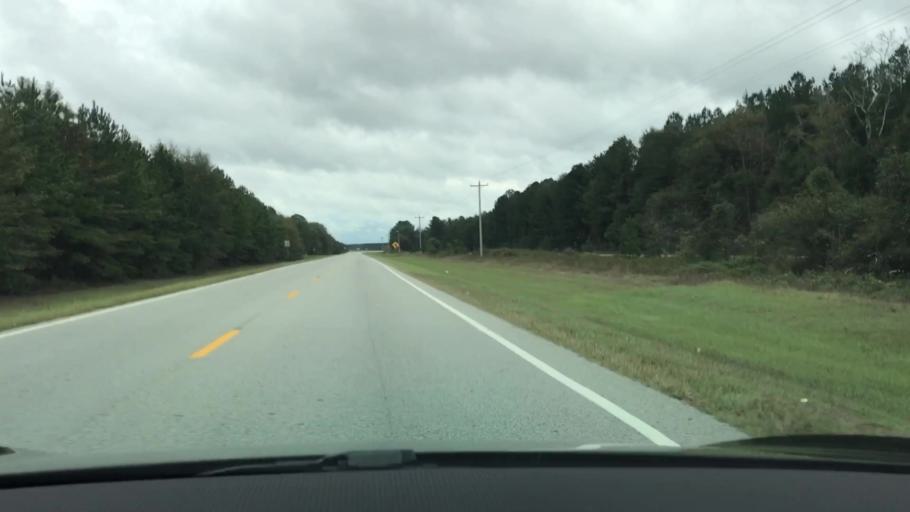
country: US
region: Georgia
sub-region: Glascock County
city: Gibson
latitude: 33.2999
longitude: -82.5182
